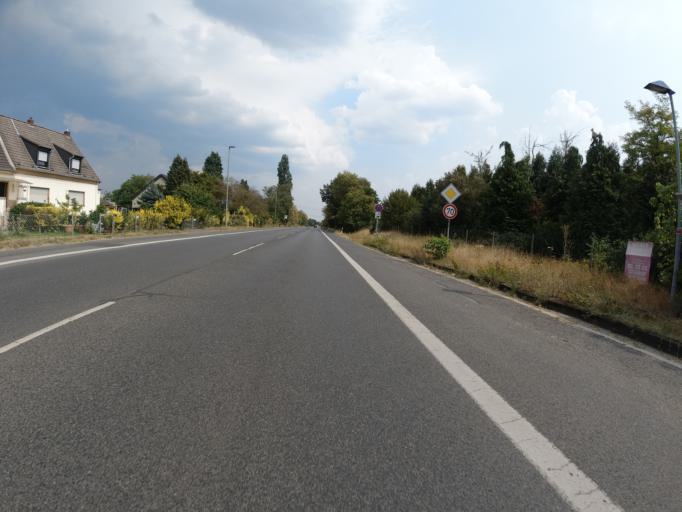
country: DE
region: North Rhine-Westphalia
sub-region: Regierungsbezirk Dusseldorf
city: Moers
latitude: 51.3940
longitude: 6.6361
